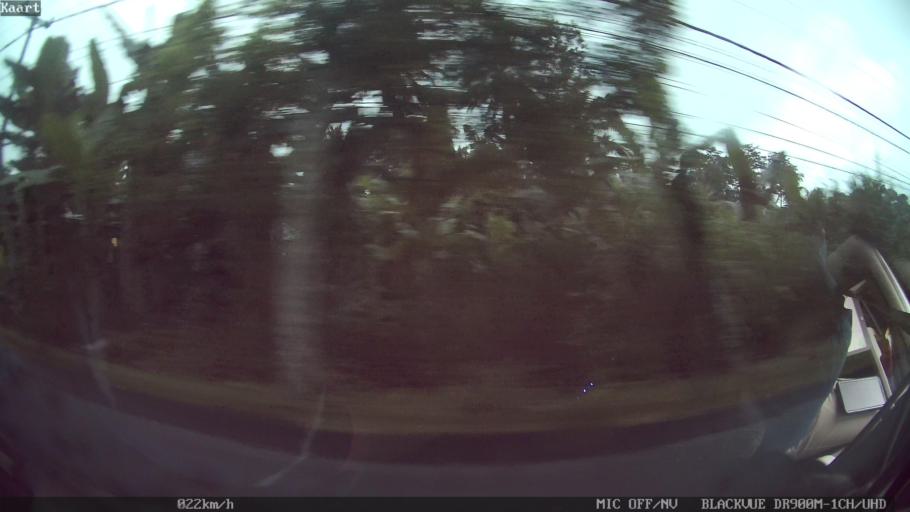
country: ID
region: Bali
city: Banjar Ponggang
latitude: -8.3906
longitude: 115.2596
